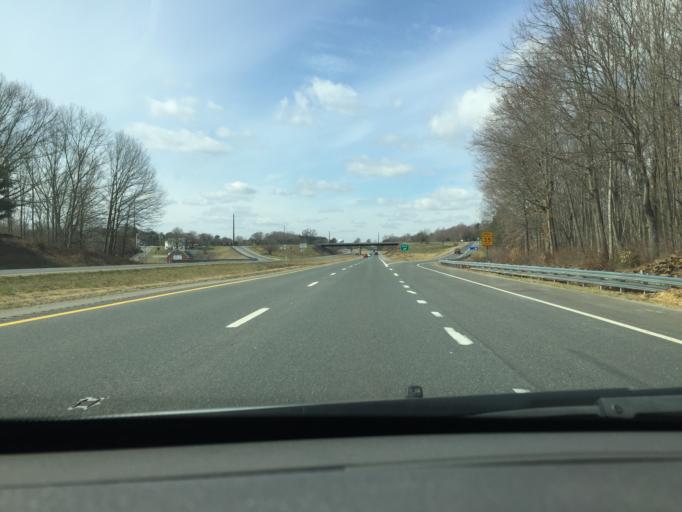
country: US
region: Virginia
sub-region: Campbell County
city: Timberlake
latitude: 37.3128
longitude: -79.2330
